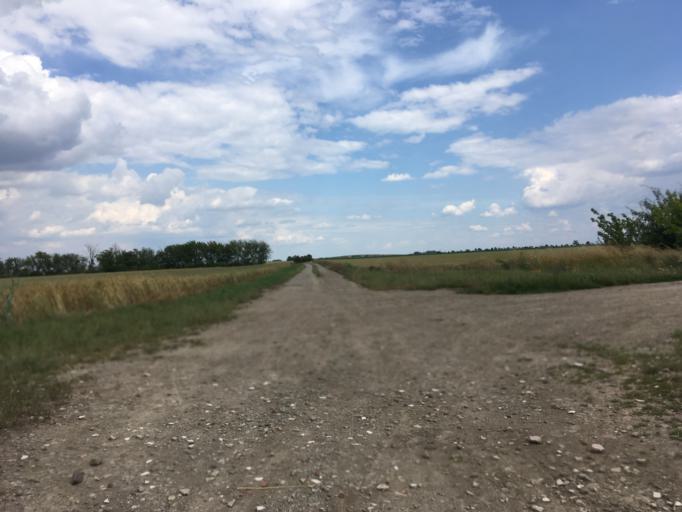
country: DE
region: Saxony-Anhalt
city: Wulfen
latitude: 51.7604
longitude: 11.8962
